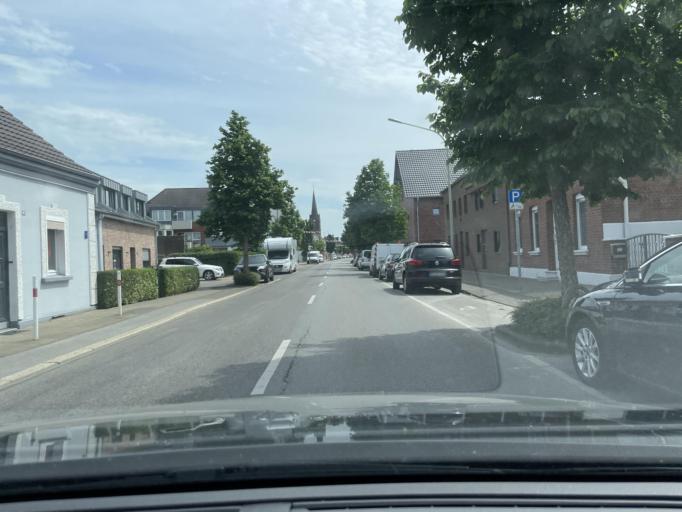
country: DE
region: North Rhine-Westphalia
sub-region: Regierungsbezirk Dusseldorf
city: Schwalmtal
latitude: 51.2069
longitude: 6.3357
